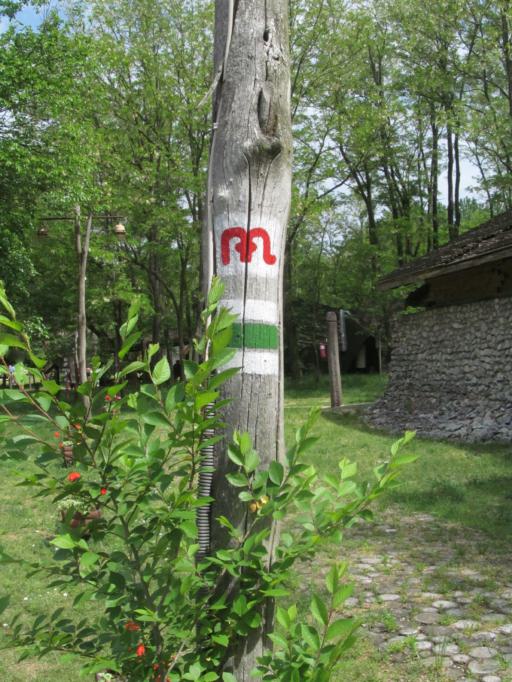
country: HU
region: Szabolcs-Szatmar-Bereg
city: Nagykallo
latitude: 47.8938
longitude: 21.8546
